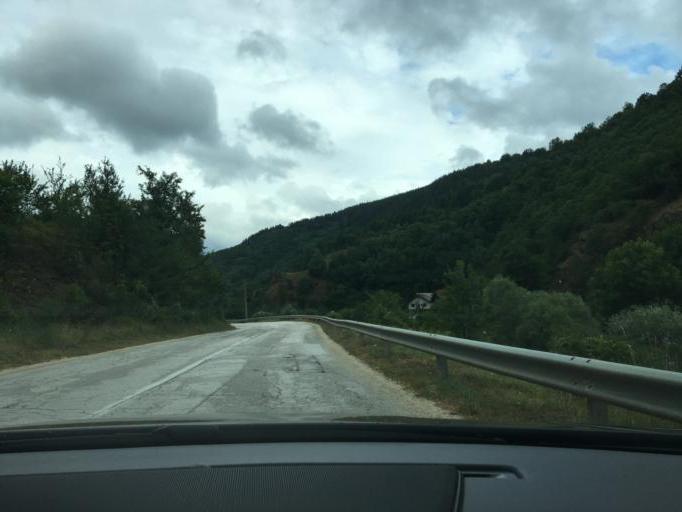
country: MK
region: Kriva Palanka
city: Kriva Palanka
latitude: 42.2236
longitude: 22.3937
